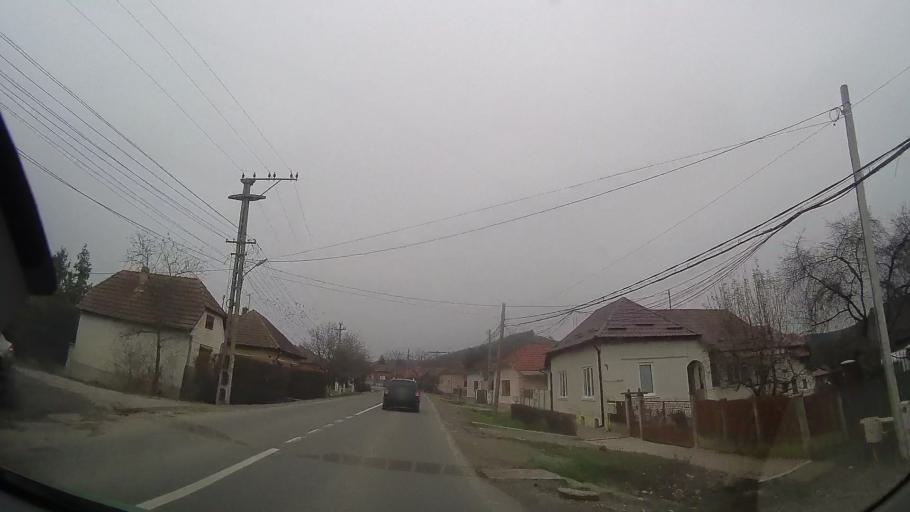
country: RO
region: Mures
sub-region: Comuna Ceausu de Campie
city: Ceausu de Campie
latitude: 46.6138
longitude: 24.5271
